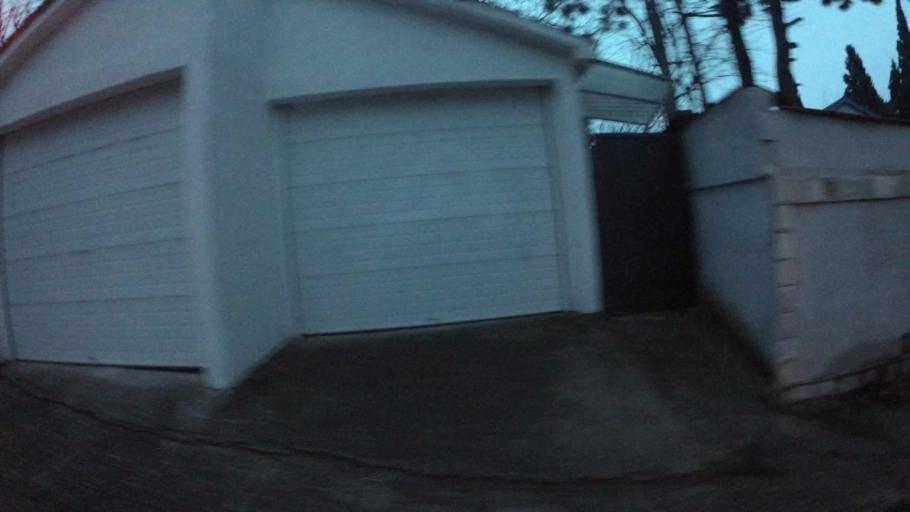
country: BA
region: Federation of Bosnia and Herzegovina
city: Rodoc
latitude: 43.3233
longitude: 17.8186
